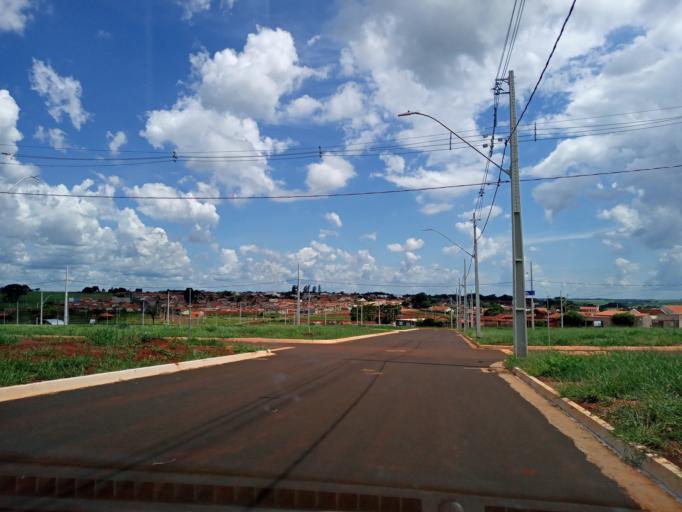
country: BR
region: Goias
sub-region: Itumbiara
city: Itumbiara
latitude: -18.4308
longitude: -49.1830
